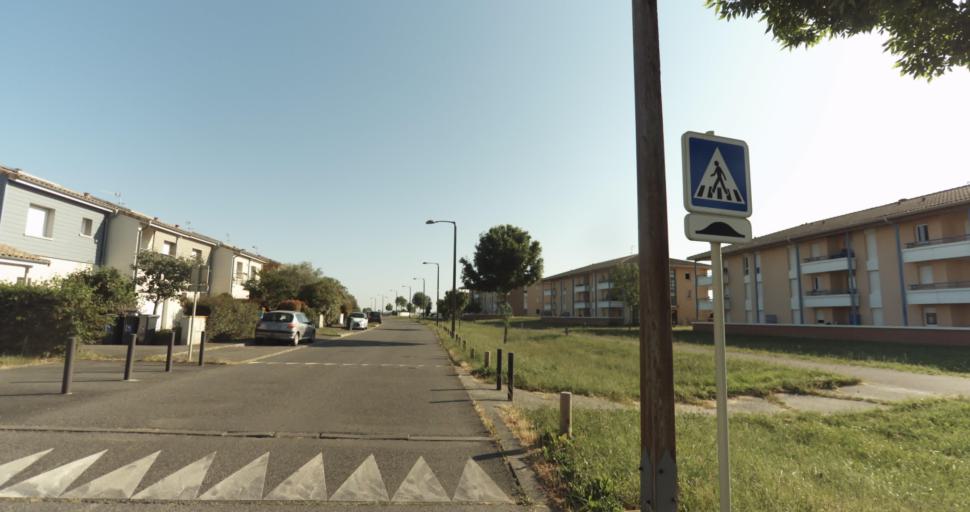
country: FR
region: Midi-Pyrenees
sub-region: Departement de la Haute-Garonne
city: La Salvetat-Saint-Gilles
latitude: 43.5730
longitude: 1.2441
